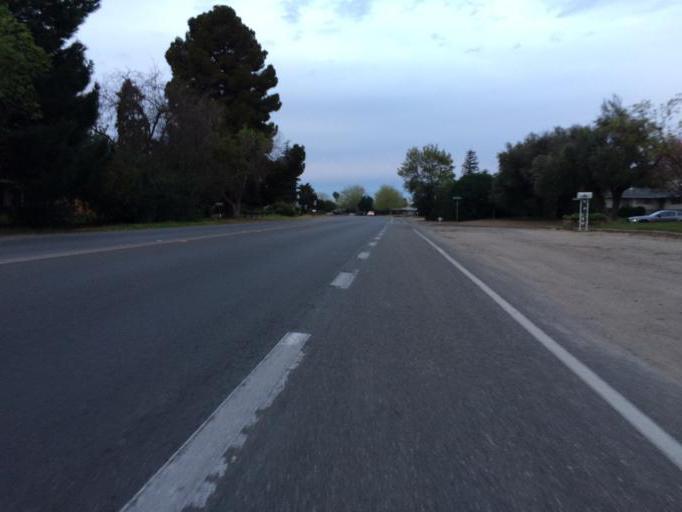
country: US
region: California
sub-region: Fresno County
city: Tarpey Village
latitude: 36.7937
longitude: -119.7051
